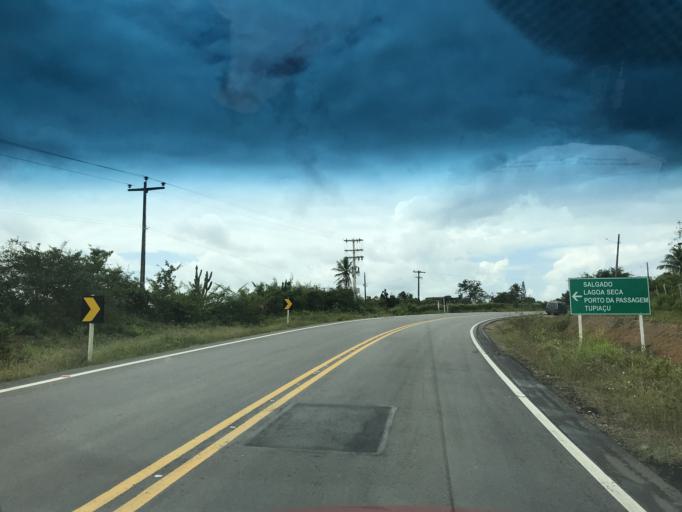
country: BR
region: Bahia
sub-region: Conceicao Do Almeida
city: Conceicao do Almeida
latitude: -12.6664
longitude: -39.2834
